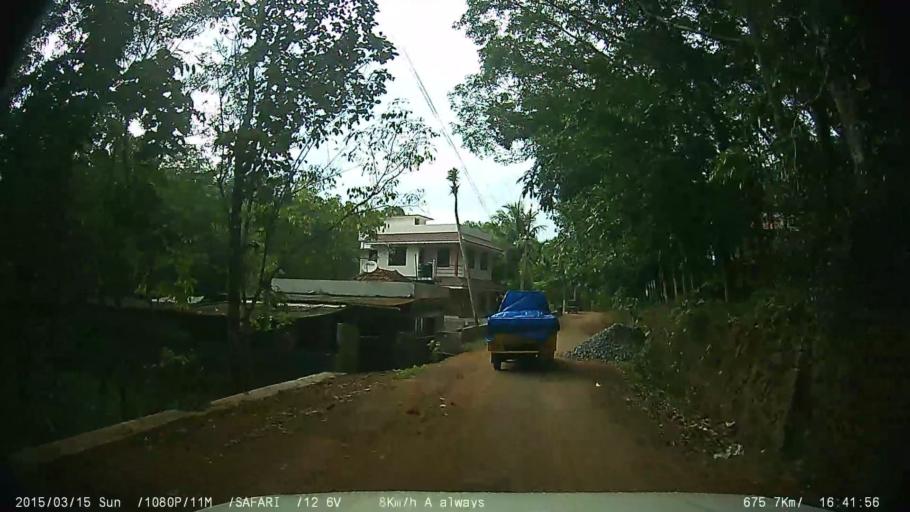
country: IN
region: Kerala
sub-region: Ernakulam
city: Piravam
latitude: 9.8550
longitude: 76.6049
